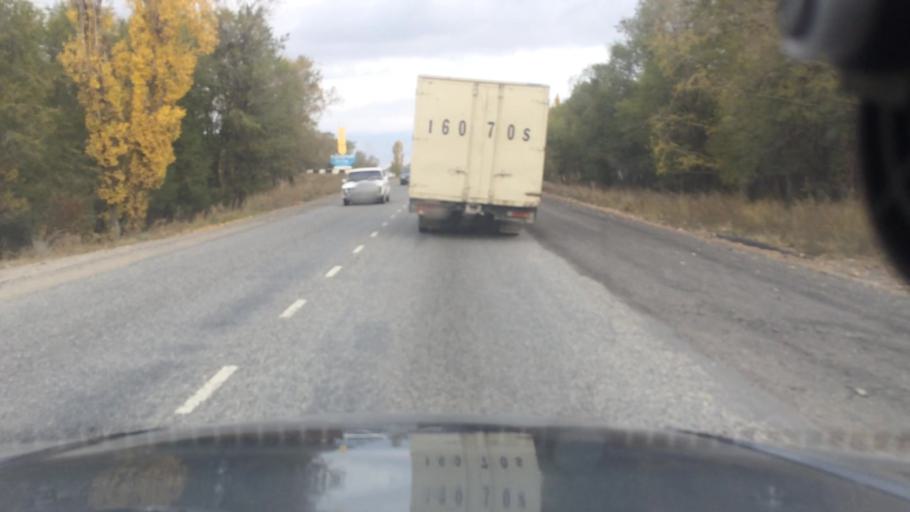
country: KG
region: Ysyk-Koel
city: Tyup
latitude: 42.6650
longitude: 78.3496
